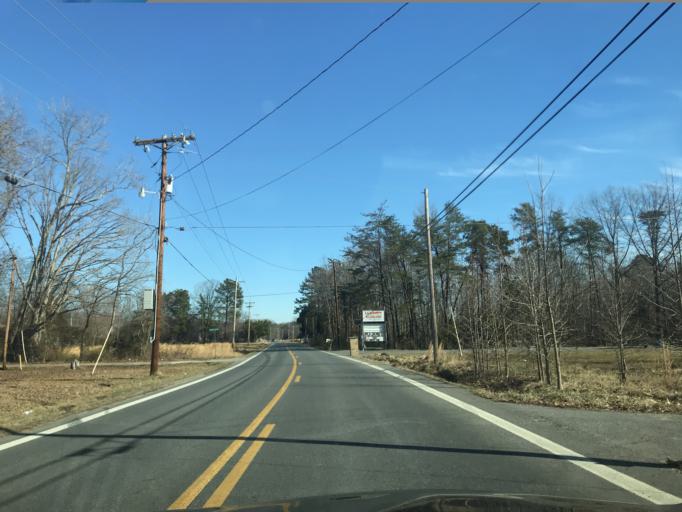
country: US
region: Maryland
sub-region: Charles County
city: Bryans Road
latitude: 38.5981
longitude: -77.0921
